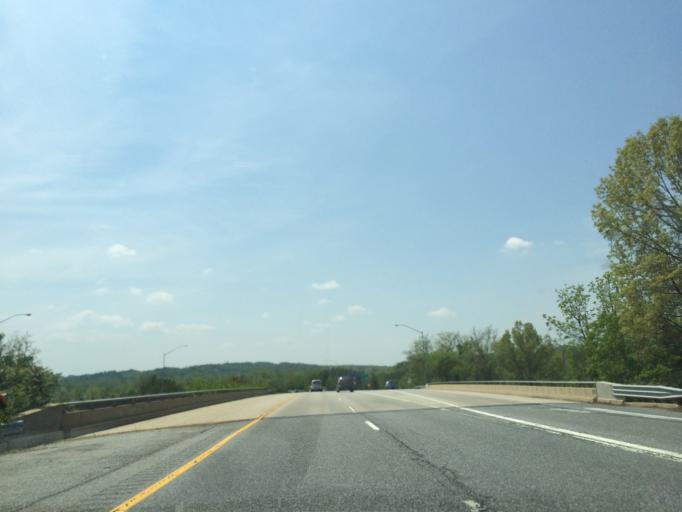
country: US
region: Maryland
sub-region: Howard County
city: Elkridge
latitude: 39.2256
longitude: -76.7019
